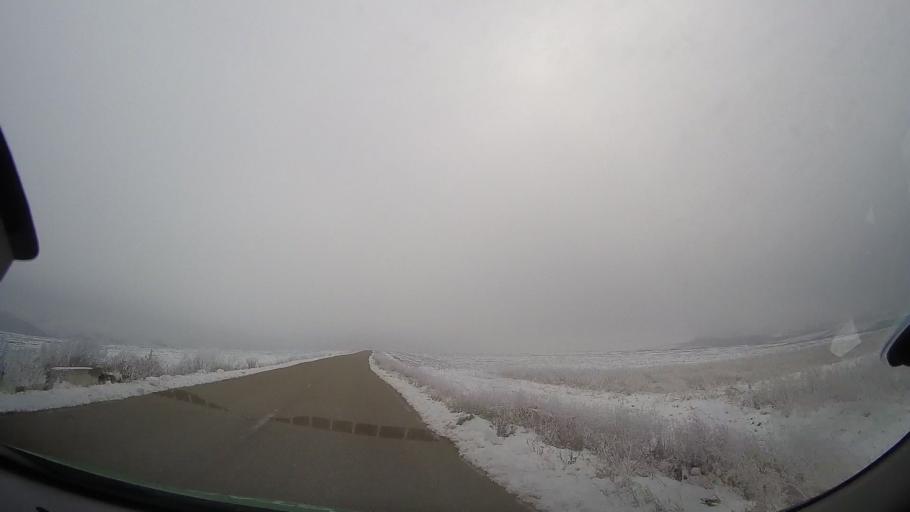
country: RO
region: Vaslui
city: Coroiesti
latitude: 46.2254
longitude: 27.4785
